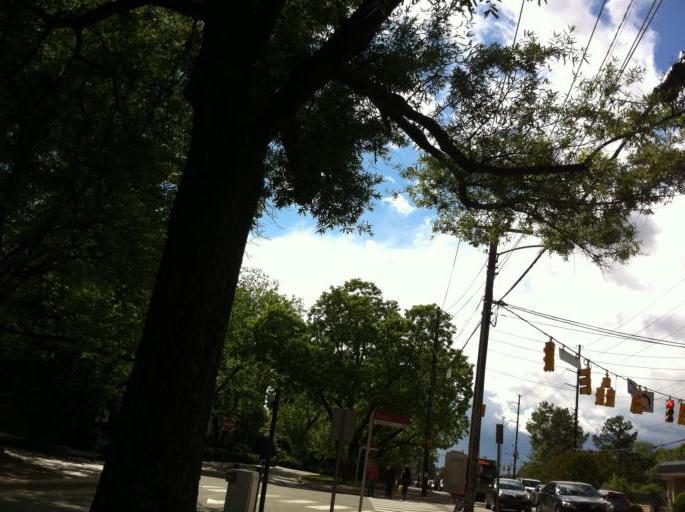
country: US
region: North Carolina
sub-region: Wake County
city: West Raleigh
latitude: 35.7887
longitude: -78.6729
